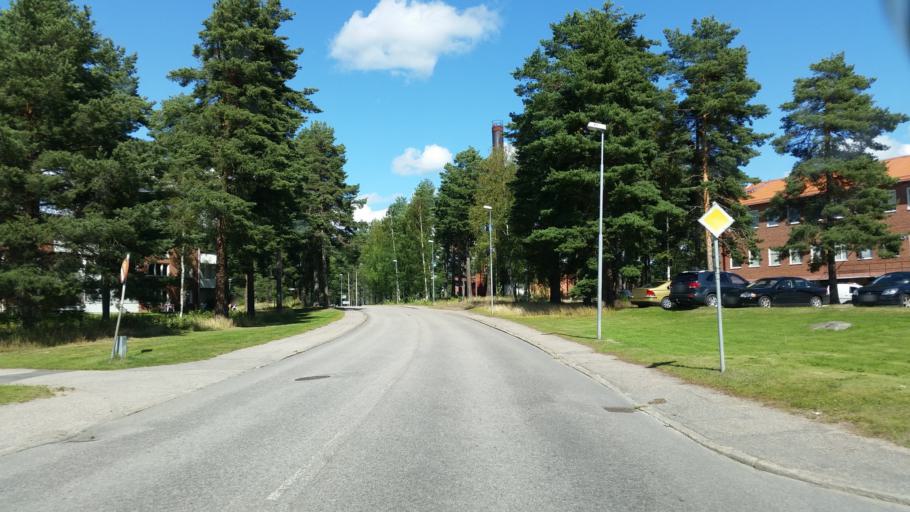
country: SE
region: Gaevleborg
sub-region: Ljusdals Kommun
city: Ljusdal
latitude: 61.8303
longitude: 16.1168
